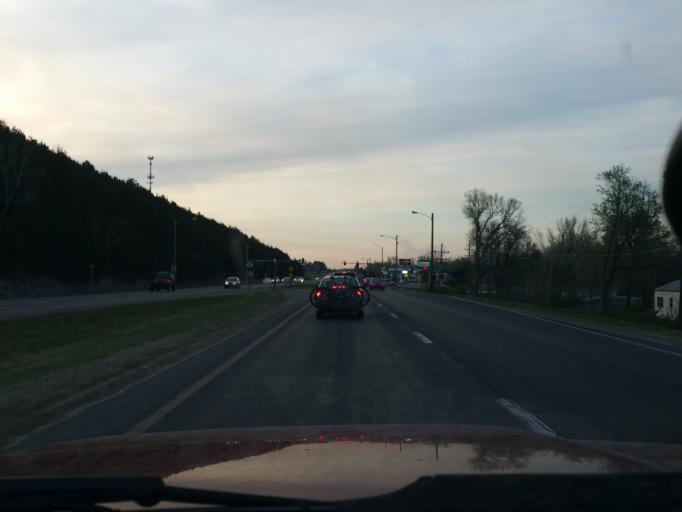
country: US
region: Kansas
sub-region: Riley County
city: Manhattan
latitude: 39.2025
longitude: -96.5659
